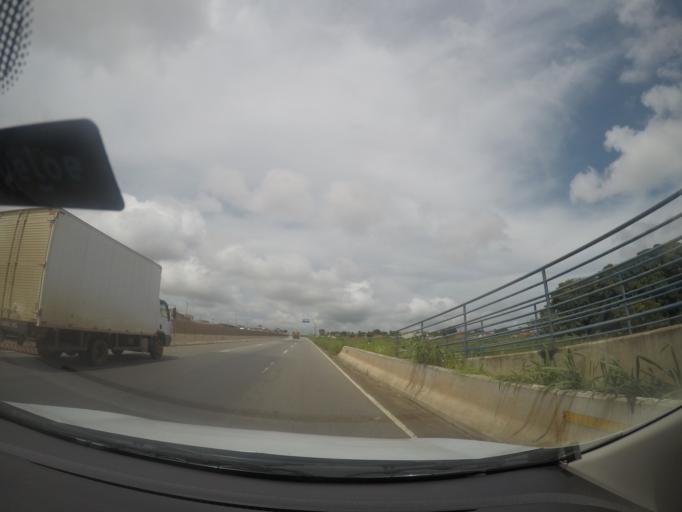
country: BR
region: Goias
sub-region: Goiania
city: Goiania
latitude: -16.7182
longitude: -49.3679
